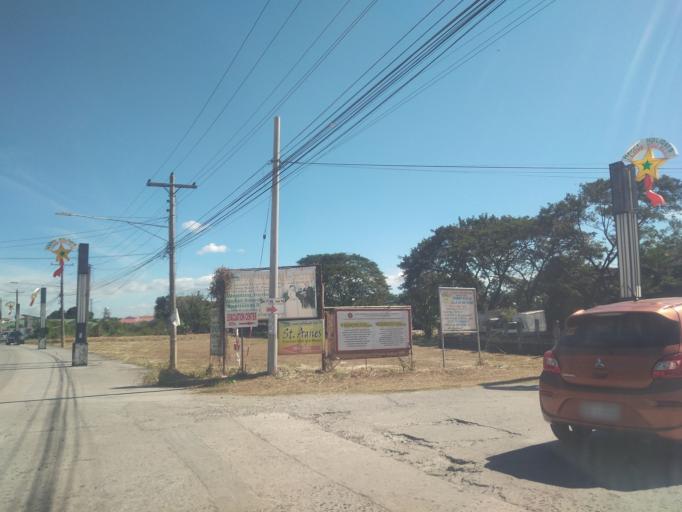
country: PH
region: Central Luzon
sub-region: Province of Pampanga
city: Bacolor
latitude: 15.0006
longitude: 120.6491
